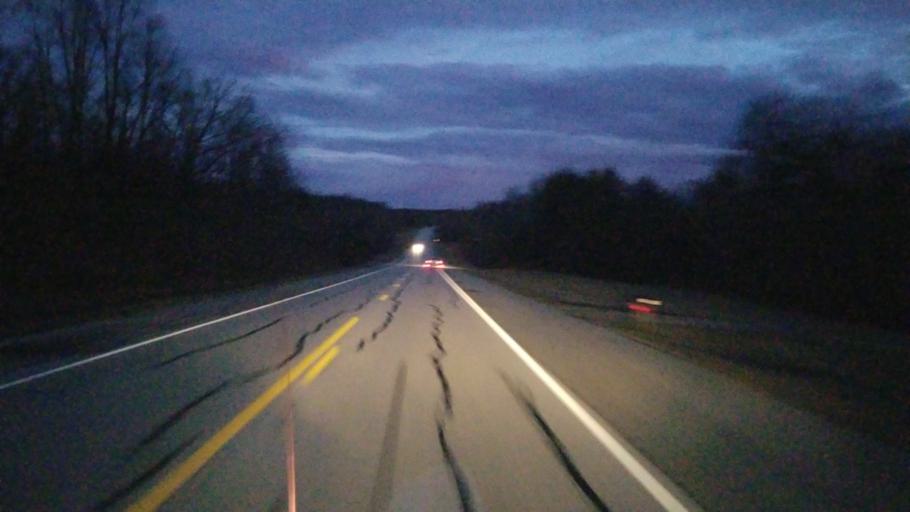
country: US
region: Tennessee
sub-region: Sequatchie County
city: Dunlap
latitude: 35.4952
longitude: -85.4726
